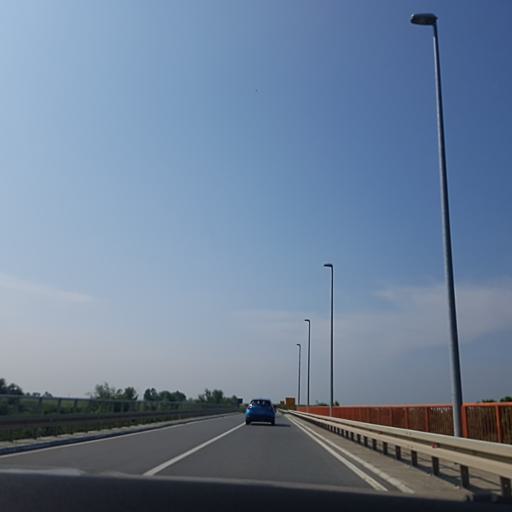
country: RS
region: Autonomna Pokrajina Vojvodina
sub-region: Srednjebanatski Okrug
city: Secanj
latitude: 45.3572
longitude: 20.7707
